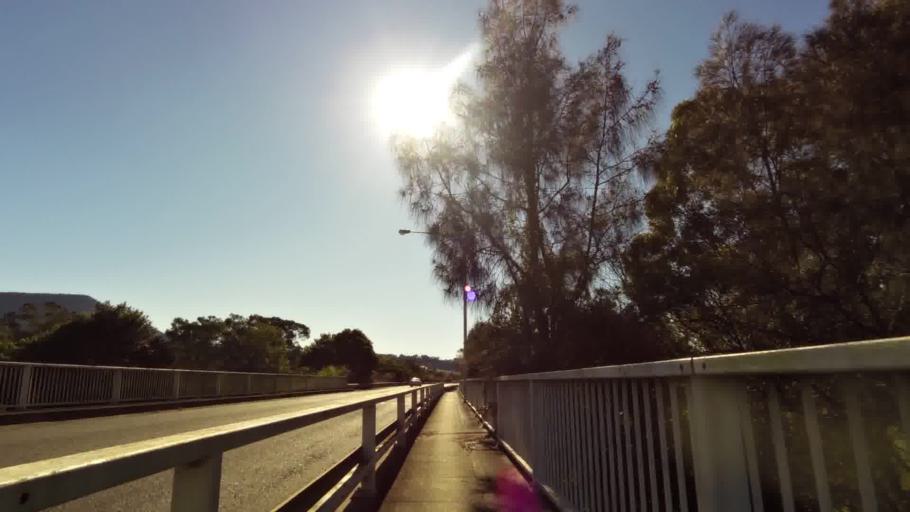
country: AU
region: New South Wales
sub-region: Wollongong
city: Koonawarra
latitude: -34.4800
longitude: 150.8049
